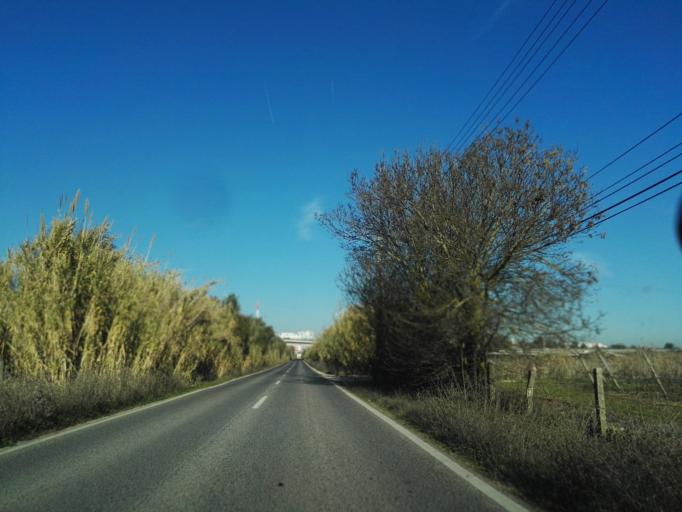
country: PT
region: Lisbon
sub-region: Alenquer
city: Carregado
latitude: 39.0158
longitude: -8.9816
